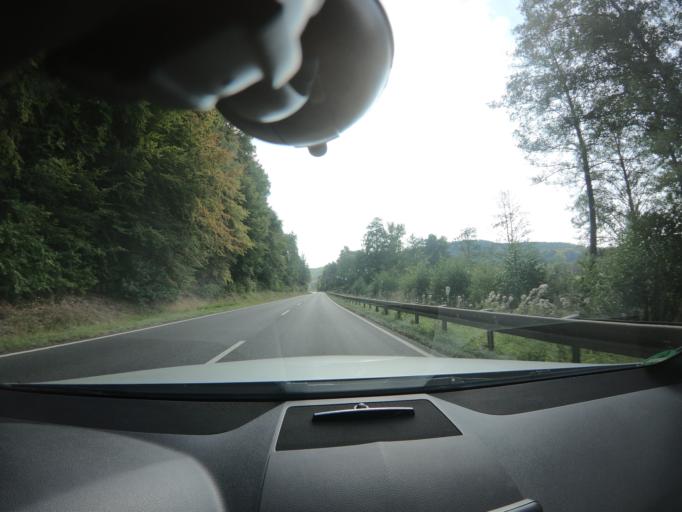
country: DE
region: Hesse
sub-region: Regierungsbezirk Giessen
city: Rauschenberg
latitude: 50.8665
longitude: 8.9337
